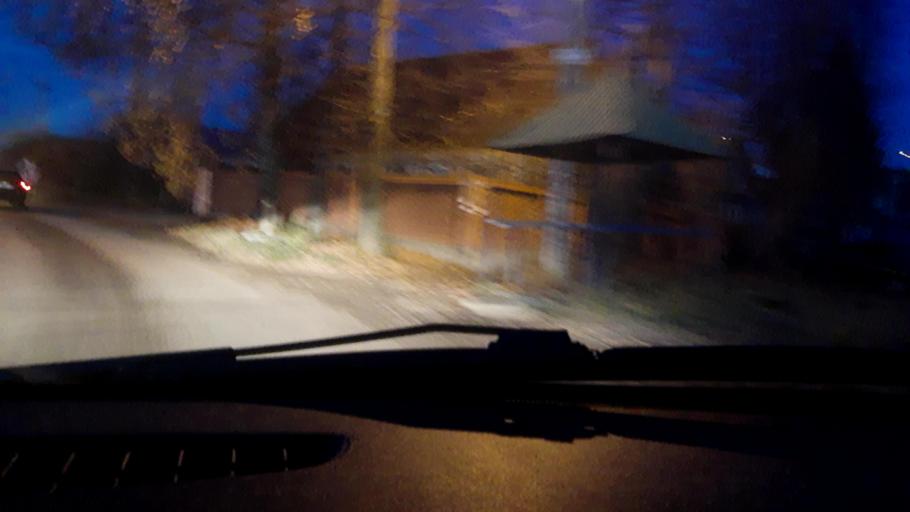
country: RU
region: Bashkortostan
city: Avdon
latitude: 54.6944
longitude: 55.8123
